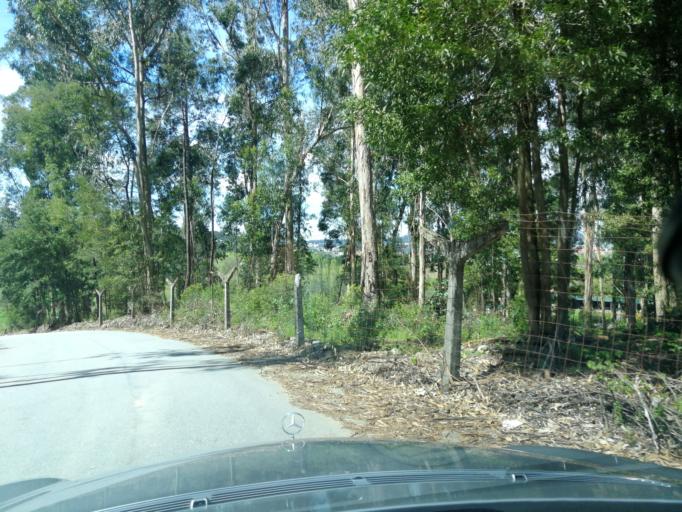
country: PT
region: Braga
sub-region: Vila Nova de Famalicao
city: Vila Nova de Famalicao
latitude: 41.4270
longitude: -8.5262
